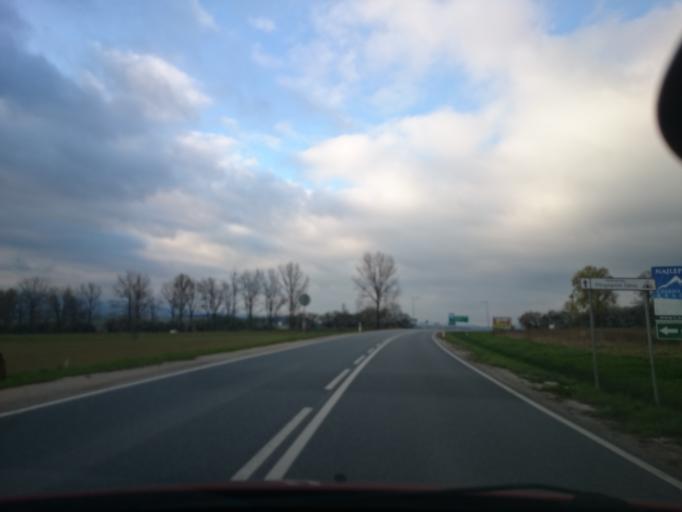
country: PL
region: Lower Silesian Voivodeship
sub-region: Powiat klodzki
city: Bystrzyca Klodzka
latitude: 50.2931
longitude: 16.6631
